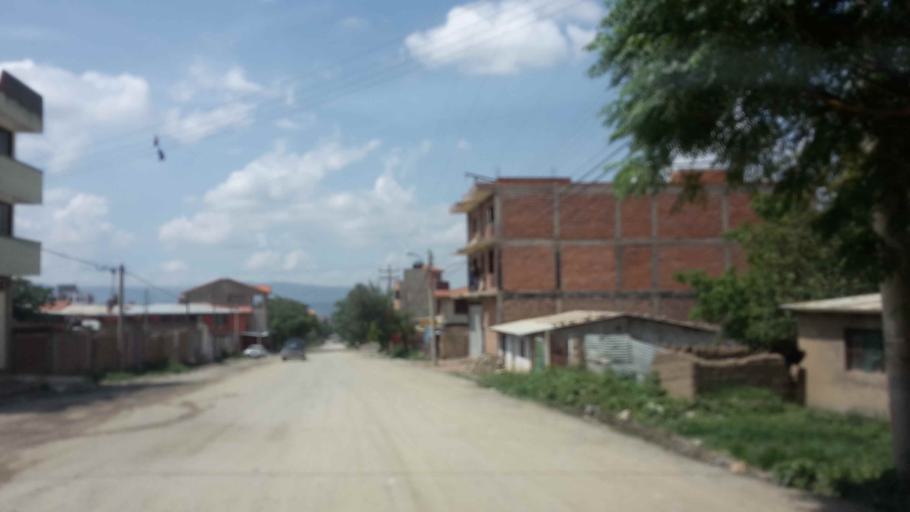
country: BO
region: Cochabamba
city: Cochabamba
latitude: -17.3315
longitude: -66.2191
